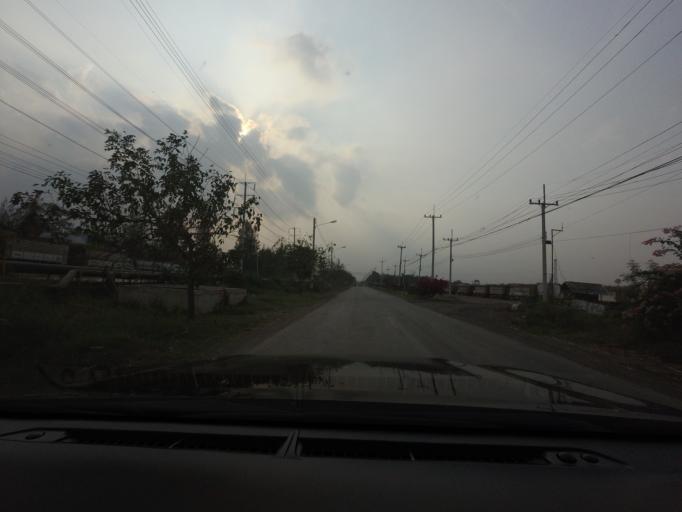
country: TH
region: Sara Buri
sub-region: Amphoe Wang Muang
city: Wang Muang
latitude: 14.8410
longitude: 101.0819
